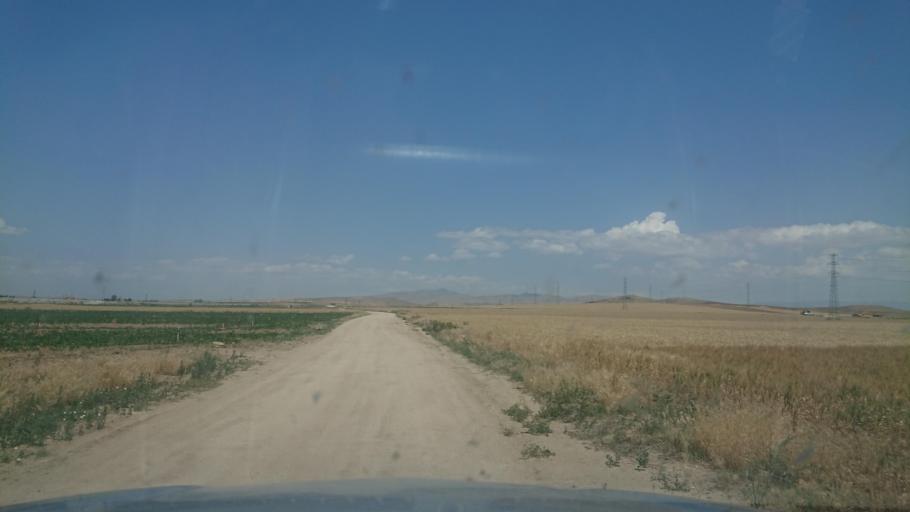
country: TR
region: Aksaray
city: Sariyahsi
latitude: 39.0158
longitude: 33.8758
